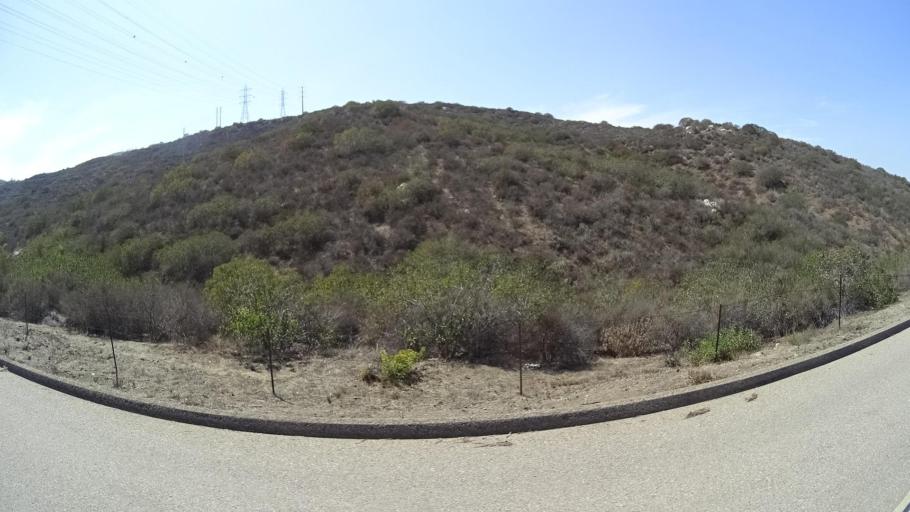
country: US
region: California
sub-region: San Diego County
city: Rancho San Diego
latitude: 32.7229
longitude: -116.9312
